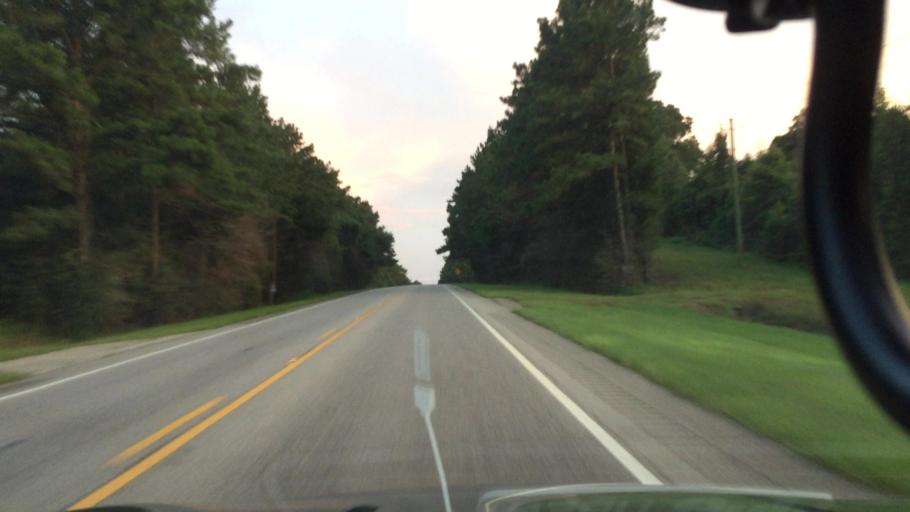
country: US
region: Alabama
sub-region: Coffee County
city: Enterprise
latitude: 31.3699
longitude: -85.8696
